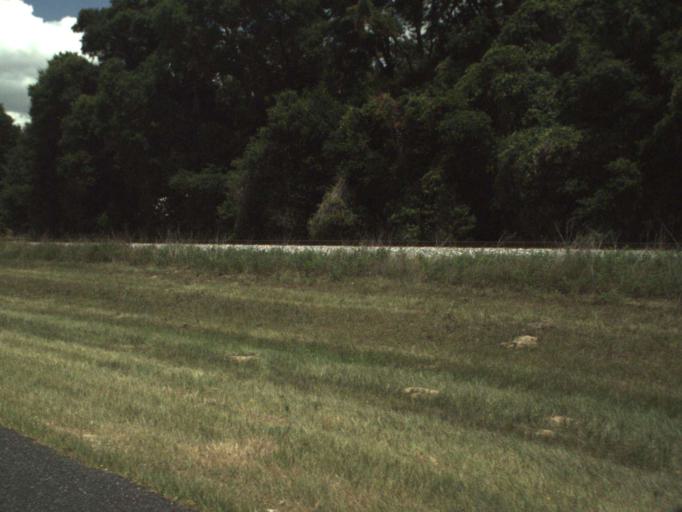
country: US
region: Florida
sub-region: Sumter County
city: The Villages
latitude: 28.9439
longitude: -82.0378
